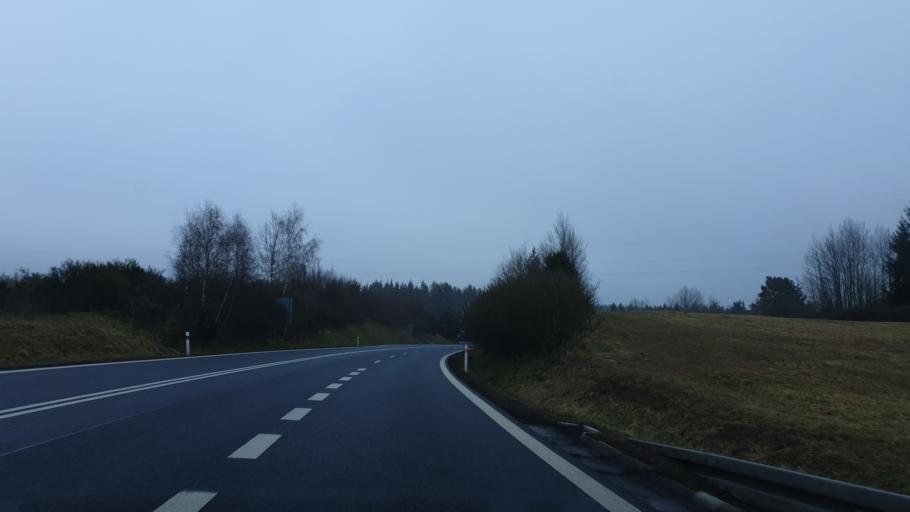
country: CZ
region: Karlovarsky
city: Hazlov
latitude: 50.1688
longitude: 12.3142
